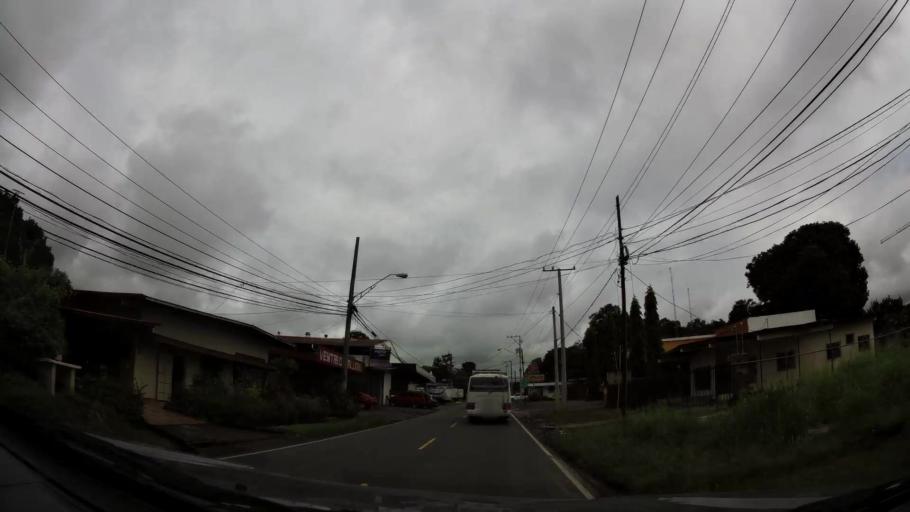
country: PA
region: Chiriqui
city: David
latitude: 8.4329
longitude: -82.4289
